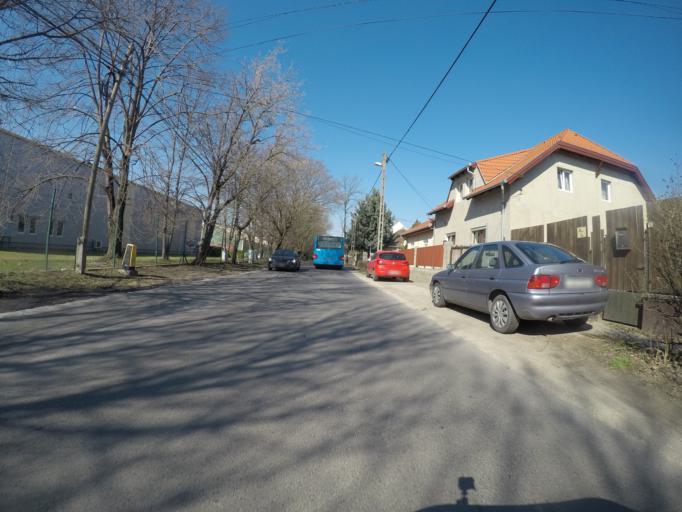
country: HU
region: Budapest
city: Budapest XIX. keruelet
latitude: 47.4372
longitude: 19.1496
